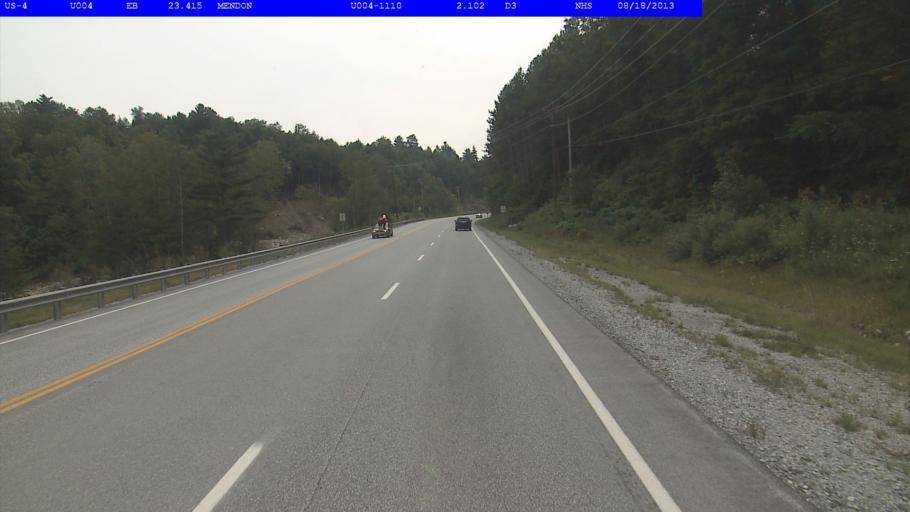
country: US
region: Vermont
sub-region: Rutland County
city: Rutland
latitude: 43.6506
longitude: -72.9114
